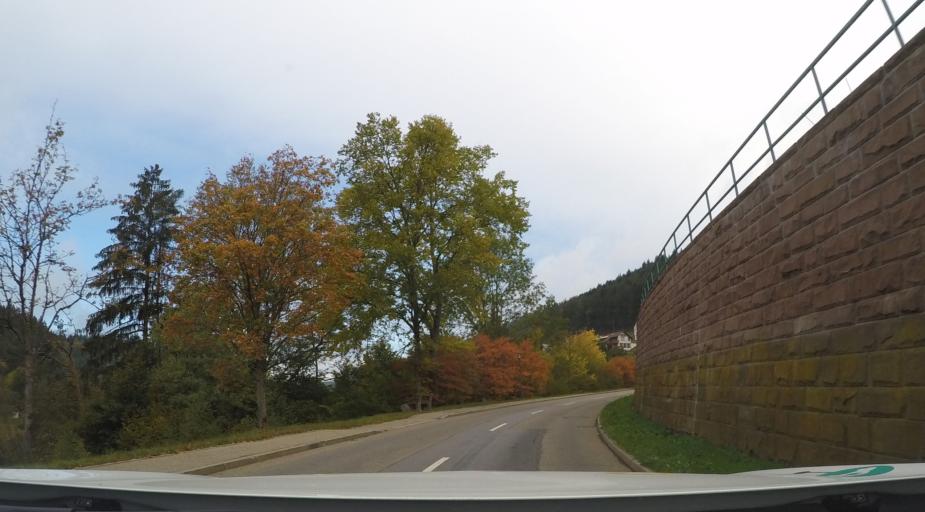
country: DE
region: Baden-Wuerttemberg
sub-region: Karlsruhe Region
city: Baiersbronn
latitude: 48.5313
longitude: 8.3614
